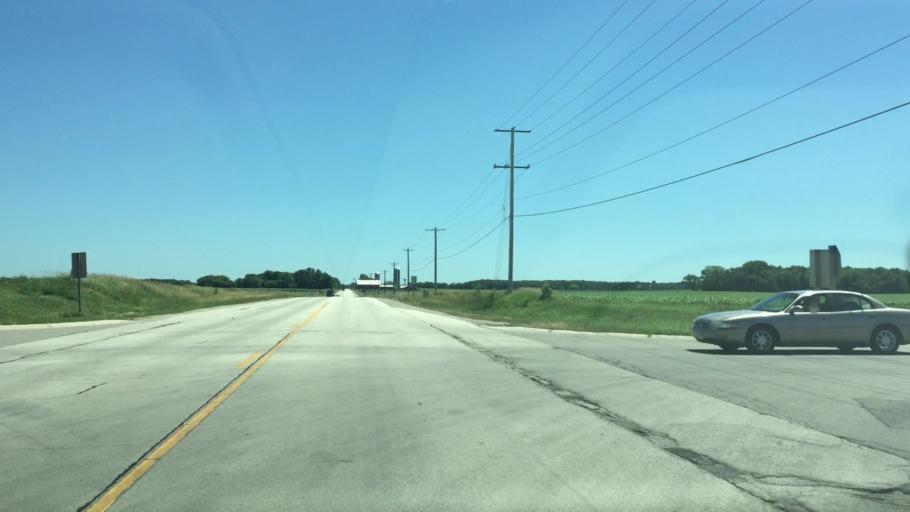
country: US
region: Wisconsin
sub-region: Calumet County
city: Hilbert
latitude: 44.1403
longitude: -88.2045
